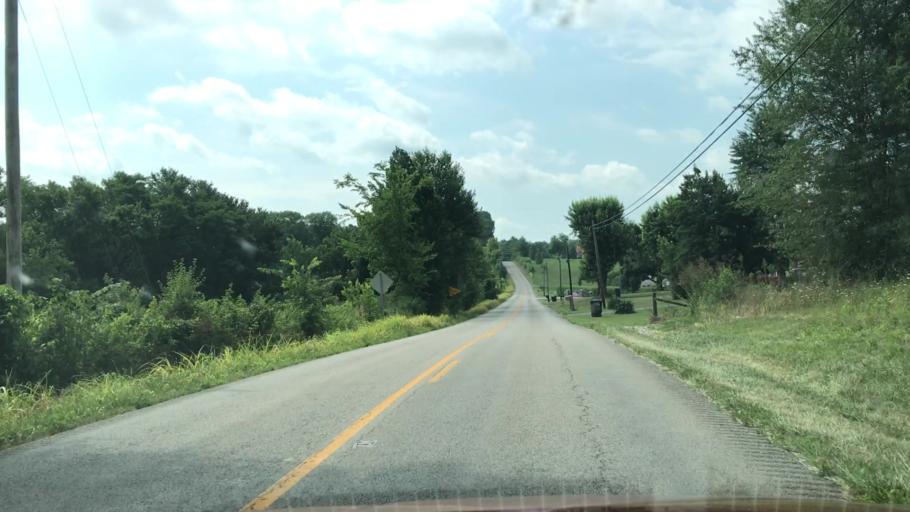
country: US
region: Kentucky
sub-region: Barren County
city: Glasgow
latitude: 36.9694
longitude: -85.8929
